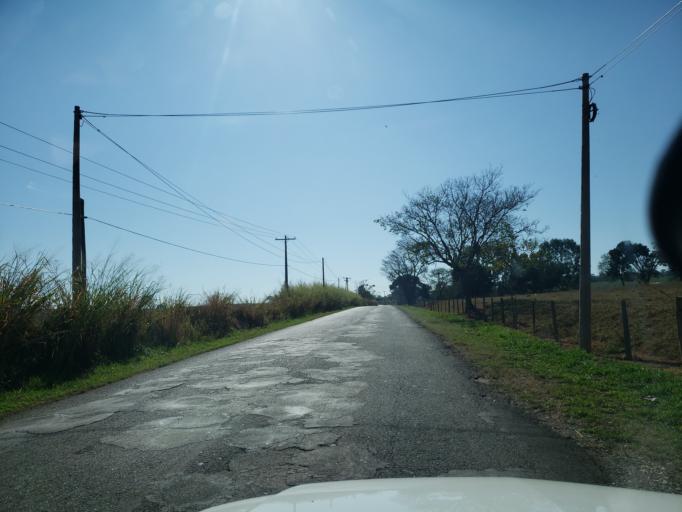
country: BR
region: Sao Paulo
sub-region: Moji-Guacu
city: Mogi-Gaucu
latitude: -22.3494
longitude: -46.8951
